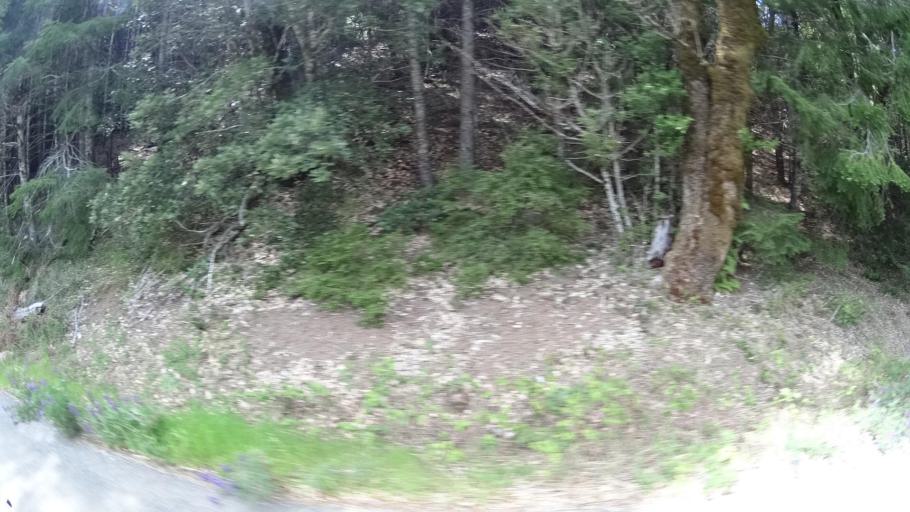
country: US
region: California
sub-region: Humboldt County
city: Redway
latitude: 40.0349
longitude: -124.0253
